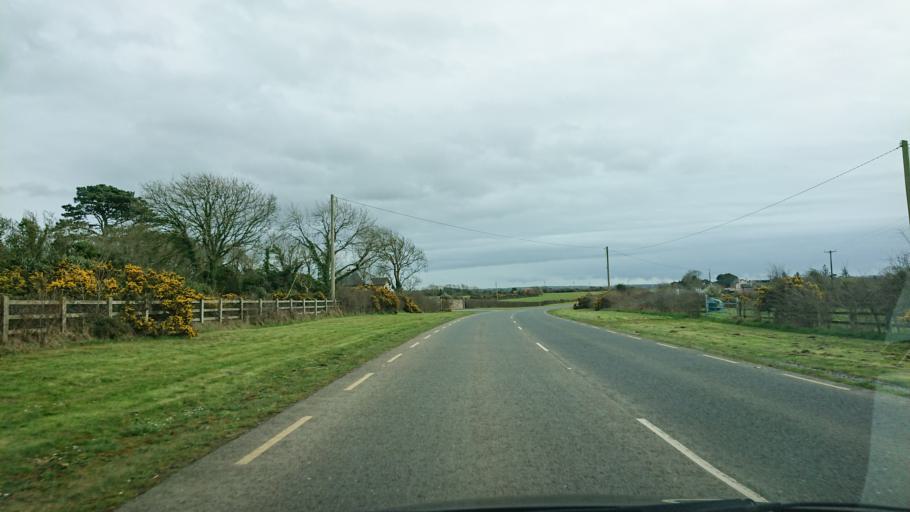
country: IE
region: Munster
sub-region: Waterford
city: Waterford
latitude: 52.2055
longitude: -7.0833
